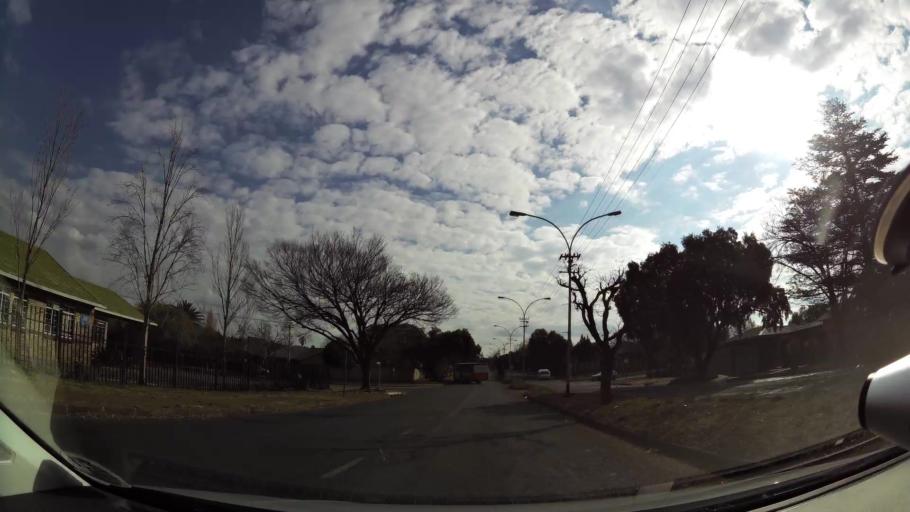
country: ZA
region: Orange Free State
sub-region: Mangaung Metropolitan Municipality
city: Bloemfontein
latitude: -29.0745
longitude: 26.2410
